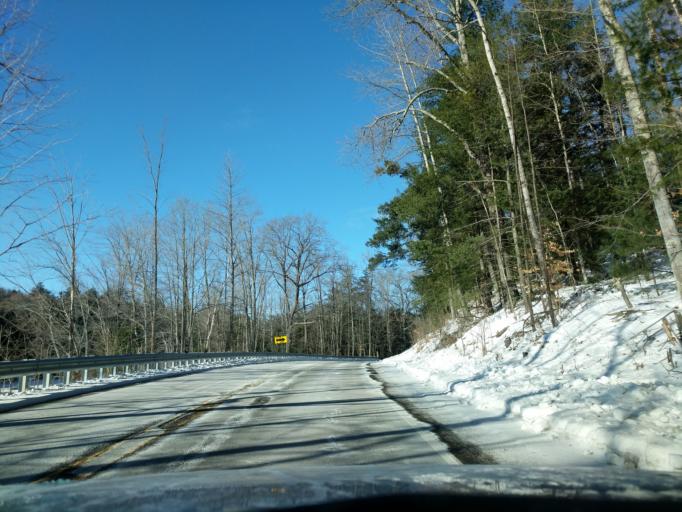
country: US
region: Wisconsin
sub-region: Menominee County
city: Keshena
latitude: 45.1048
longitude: -88.6370
